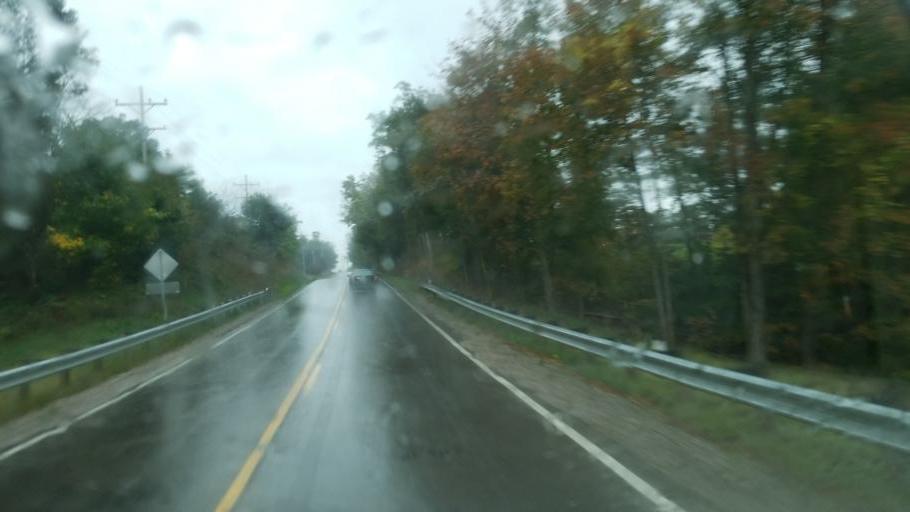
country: US
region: Ohio
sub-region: Richland County
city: Lincoln Heights
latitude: 40.8243
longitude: -82.4810
